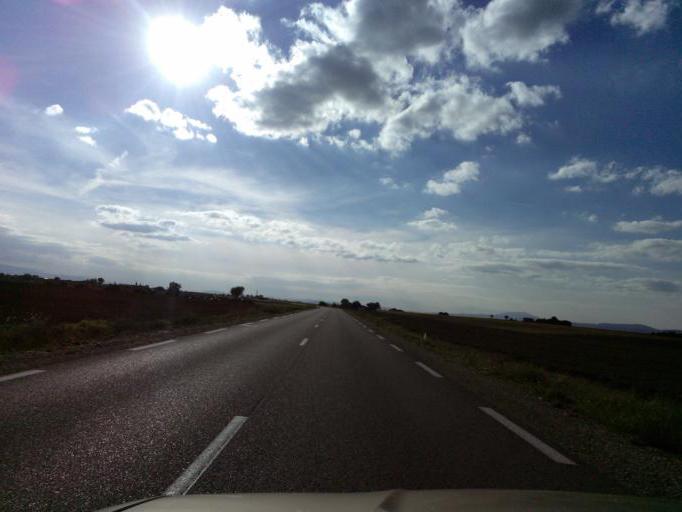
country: FR
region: Provence-Alpes-Cote d'Azur
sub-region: Departement des Alpes-de-Haute-Provence
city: Valensole
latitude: 43.8296
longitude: 5.9476
